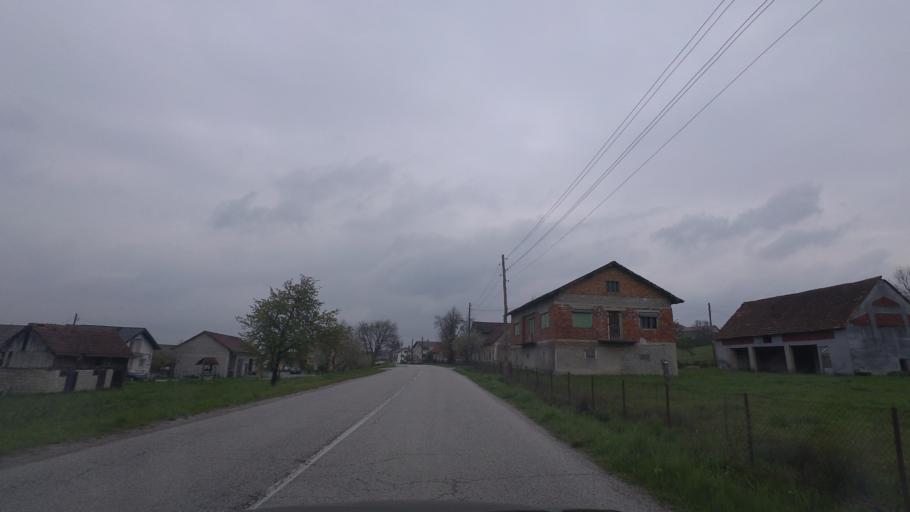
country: HR
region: Zagrebacka
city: Jastrebarsko
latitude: 45.6165
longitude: 15.5796
